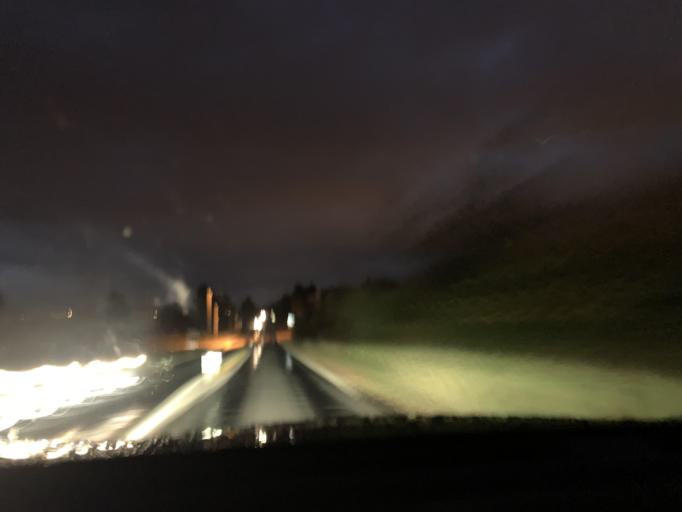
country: FR
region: Rhone-Alpes
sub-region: Departement du Rhone
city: Lucenay
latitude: 45.9313
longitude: 4.6864
